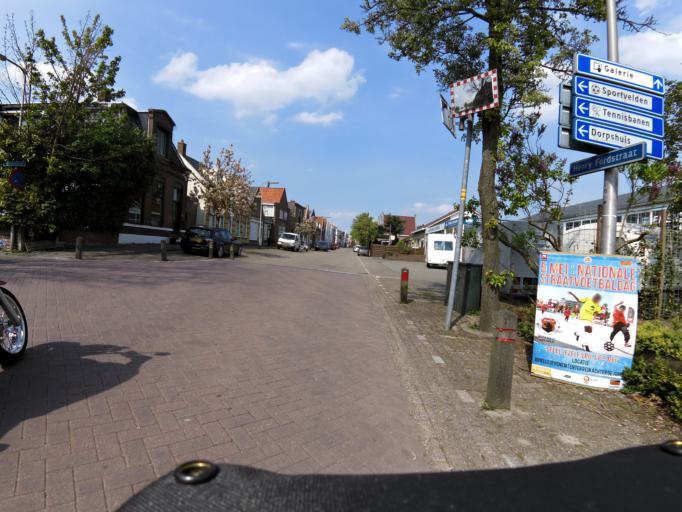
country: NL
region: South Holland
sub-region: Gemeente Maassluis
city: Maassluis
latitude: 51.8805
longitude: 4.2225
